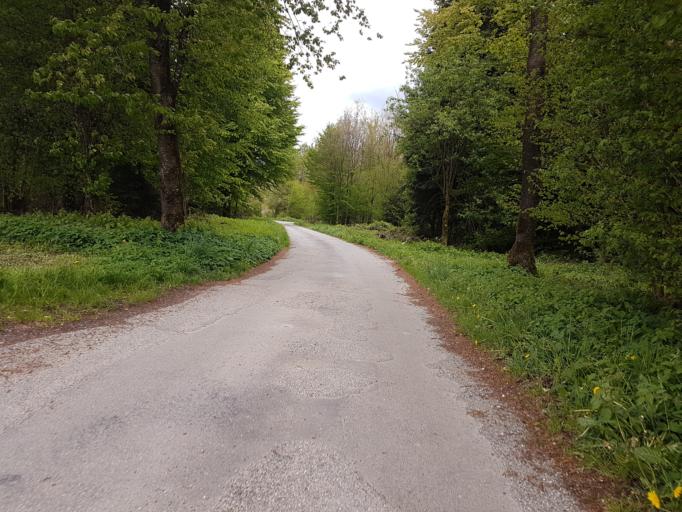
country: CH
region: Bern
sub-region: Oberaargau
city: Aarwangen
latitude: 47.2387
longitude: 7.7535
